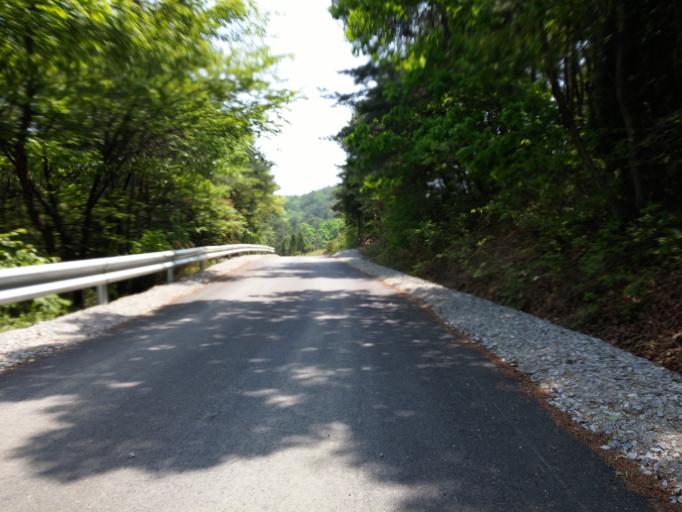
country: KR
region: Chungcheongbuk-do
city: Okcheon
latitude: 36.4254
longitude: 127.5842
